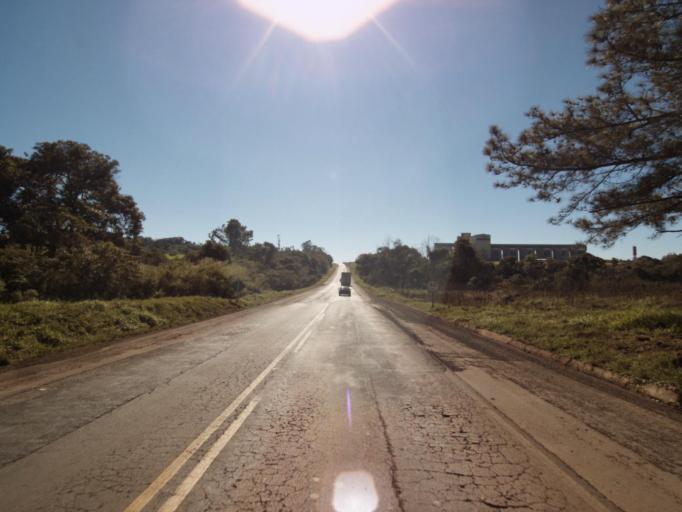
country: BR
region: Rio Grande do Sul
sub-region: Frederico Westphalen
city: Frederico Westphalen
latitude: -26.9117
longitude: -53.1877
